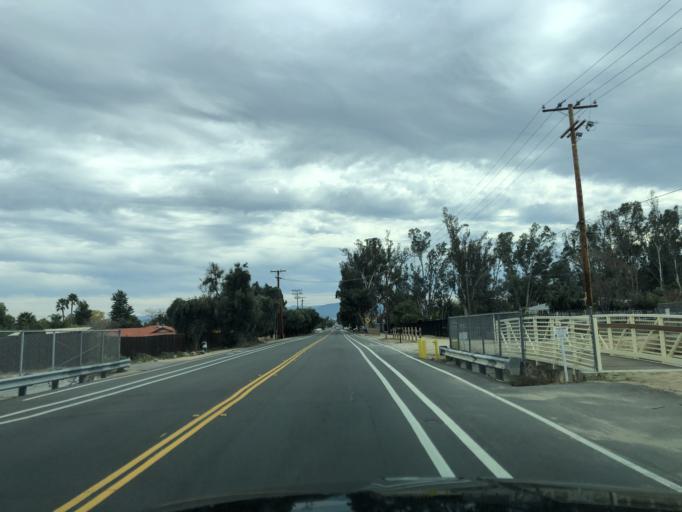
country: US
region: California
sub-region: Riverside County
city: Wildomar
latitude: 33.6014
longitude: -117.2839
